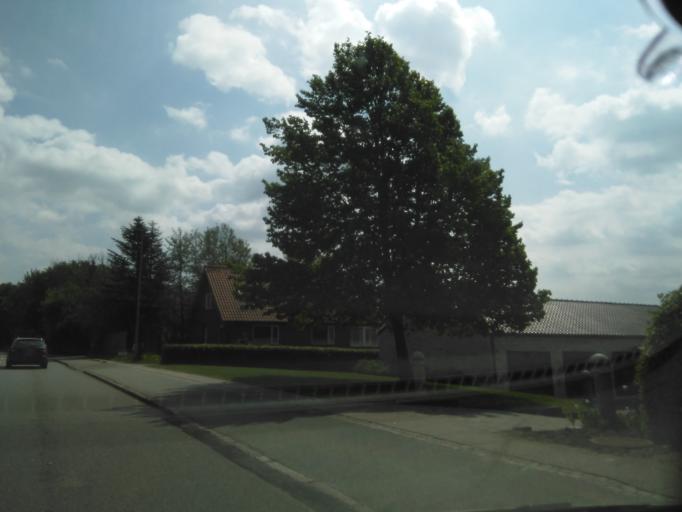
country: DK
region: Central Jutland
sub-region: Skanderborg Kommune
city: Skanderborg
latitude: 56.0351
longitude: 9.9492
